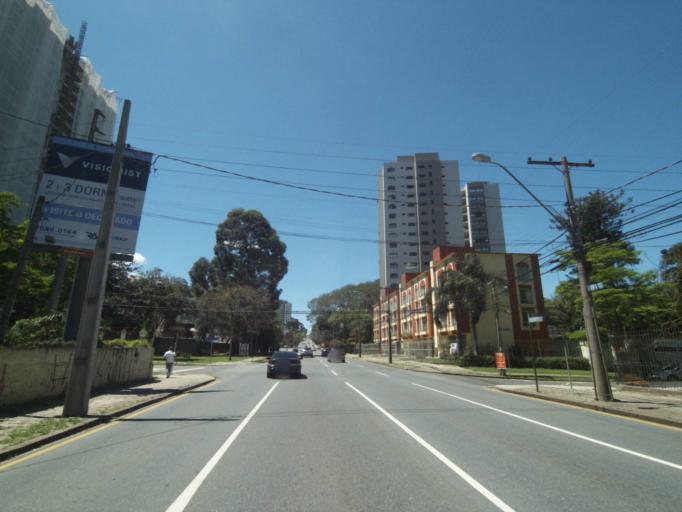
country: BR
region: Parana
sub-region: Curitiba
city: Curitiba
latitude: -25.4061
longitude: -49.2508
